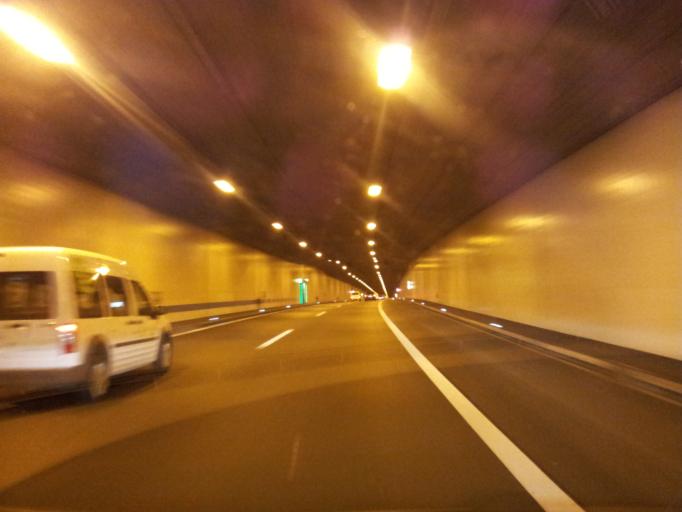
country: CH
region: Lucerne
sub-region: Lucerne-Land District
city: Horw
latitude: 47.0144
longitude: 8.3031
